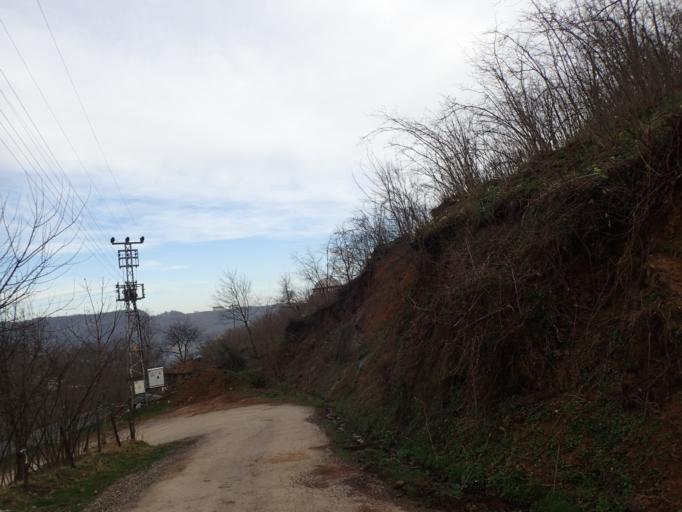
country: TR
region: Ordu
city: Camas
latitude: 40.8898
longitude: 37.5115
